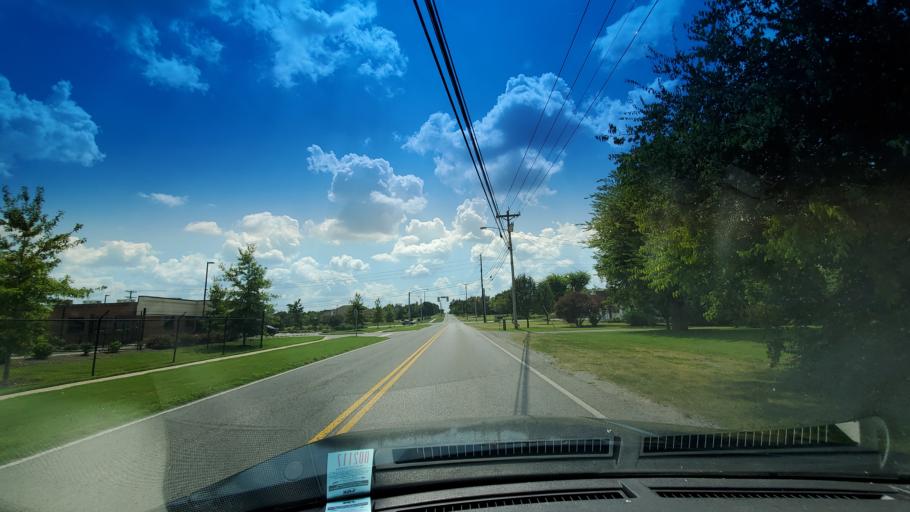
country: US
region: Tennessee
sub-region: Wilson County
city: Lebanon
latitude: 36.1750
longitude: -86.3086
